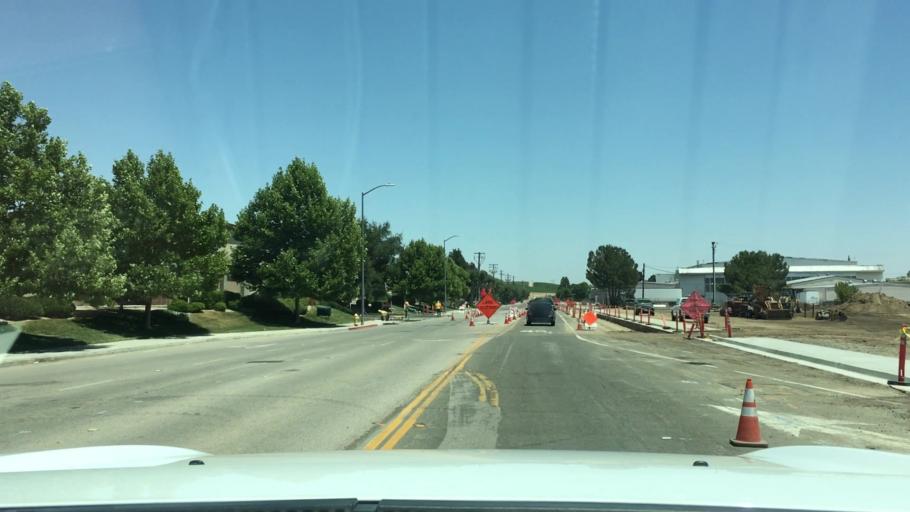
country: US
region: California
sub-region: San Luis Obispo County
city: Paso Robles
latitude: 35.6157
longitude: -120.6587
